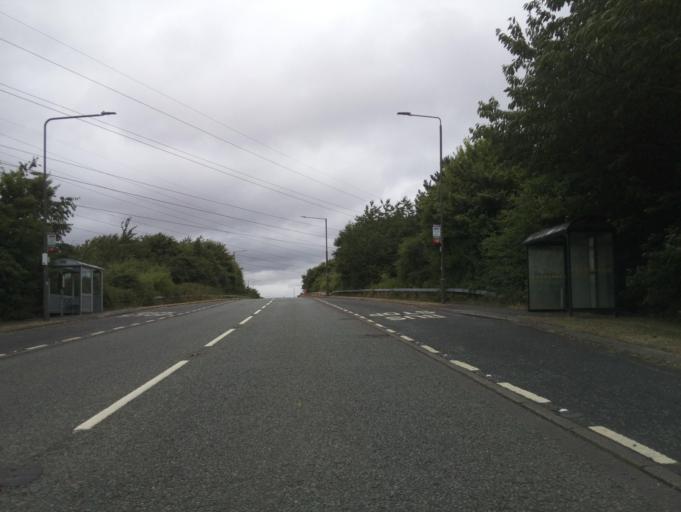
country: GB
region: England
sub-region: Derbyshire
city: Findern
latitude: 52.8653
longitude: -1.5462
